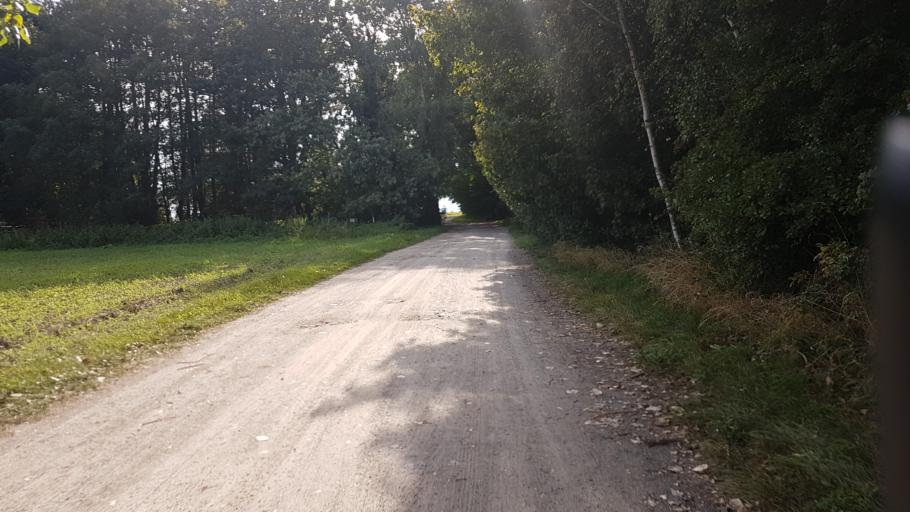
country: DE
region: Mecklenburg-Vorpommern
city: Altefahr
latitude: 54.4459
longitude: 13.1279
